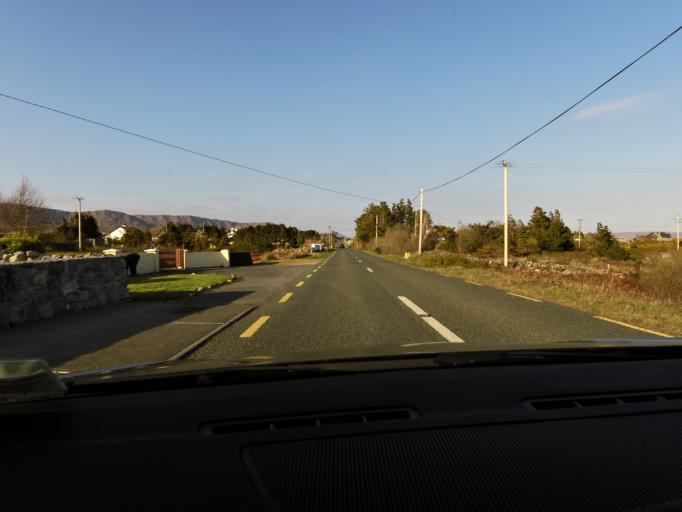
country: IE
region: Connaught
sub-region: County Galway
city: Clifden
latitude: 53.3341
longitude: -9.7261
